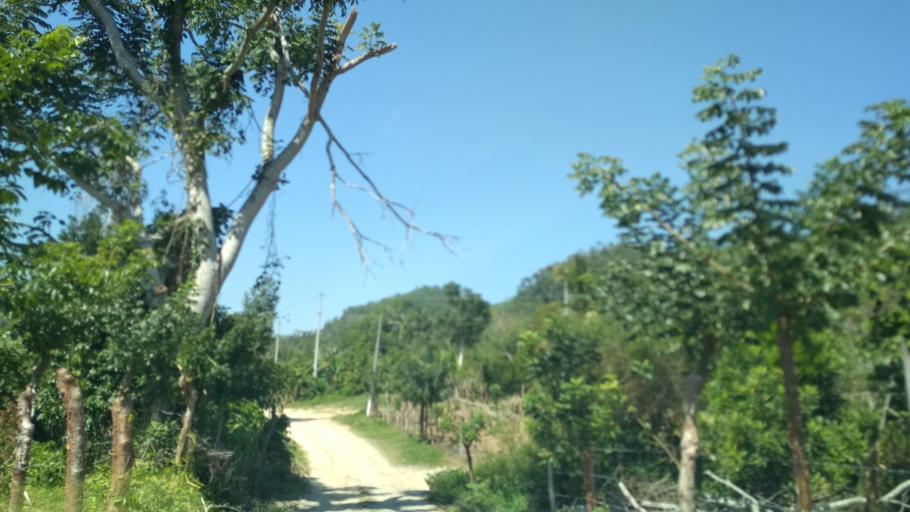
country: MX
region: Veracruz
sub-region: Papantla
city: Polutla
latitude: 20.4803
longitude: -97.2226
